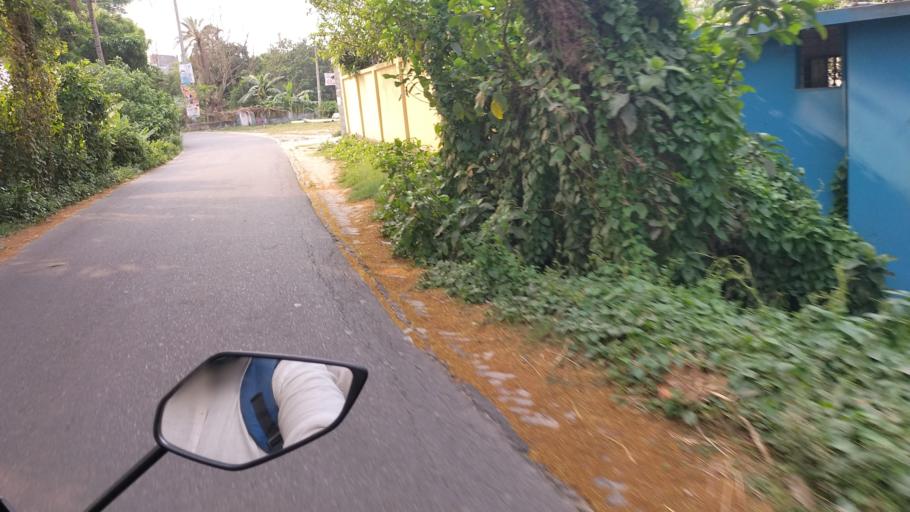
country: BD
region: Dhaka
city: Azimpur
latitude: 23.6696
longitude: 90.3458
